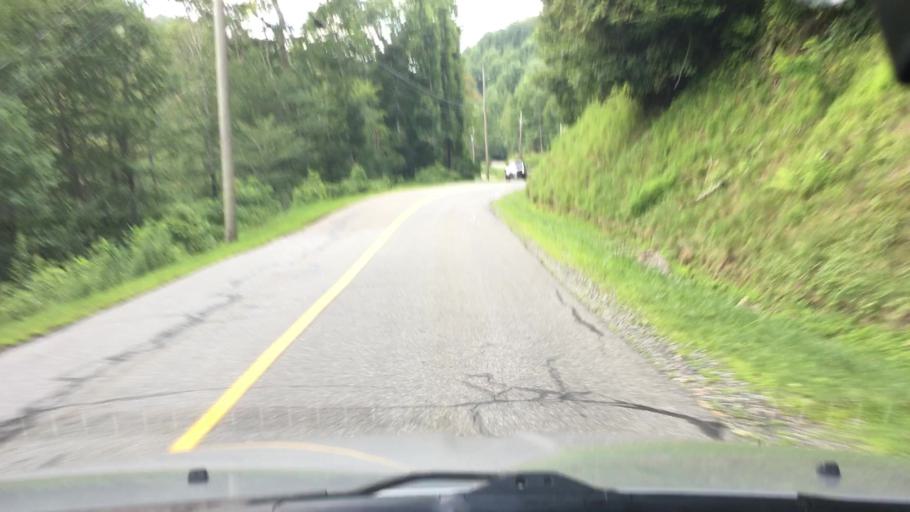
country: US
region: North Carolina
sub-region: Madison County
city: Mars Hill
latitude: 35.9575
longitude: -82.5142
